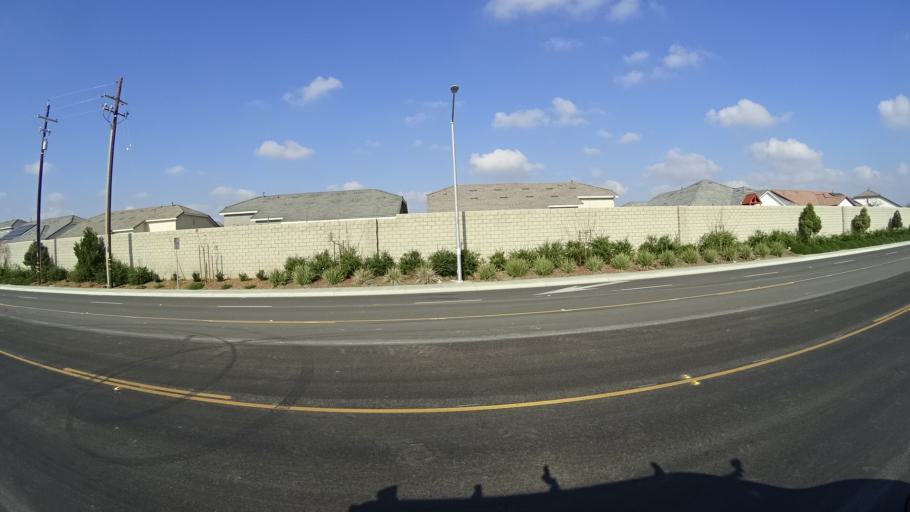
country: US
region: California
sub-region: Kern County
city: Greenacres
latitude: 35.2888
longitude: -119.1115
